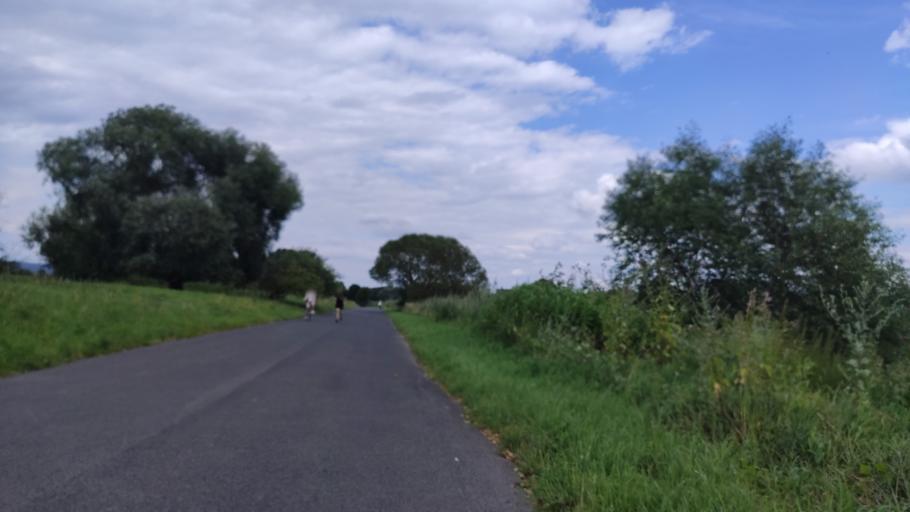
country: DE
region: North Rhine-Westphalia
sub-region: Regierungsbezirk Detmold
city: Hoexter
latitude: 51.7914
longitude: 9.4169
